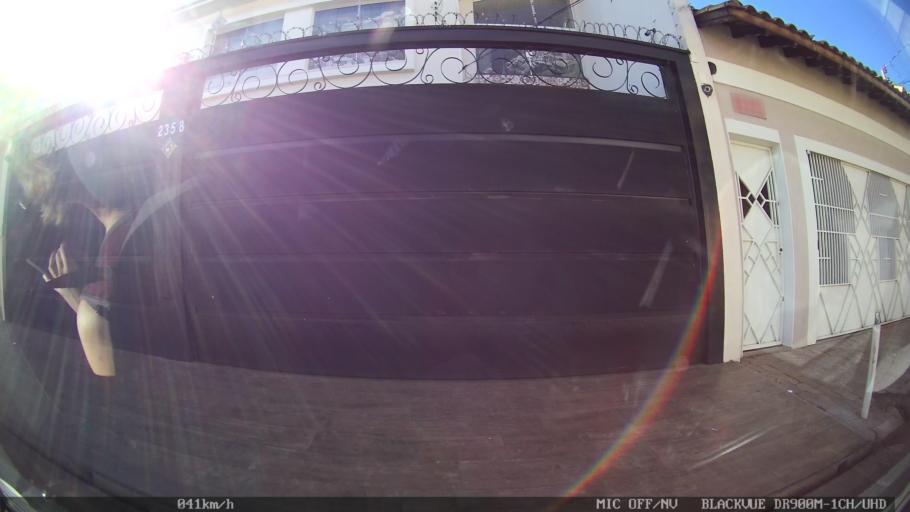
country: BR
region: Sao Paulo
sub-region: Franca
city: Franca
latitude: -20.5331
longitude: -47.4001
